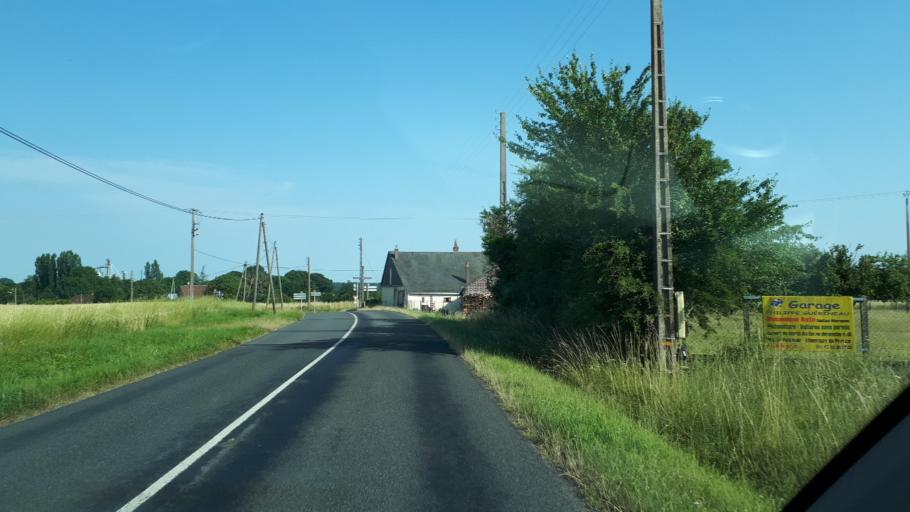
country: FR
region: Centre
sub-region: Departement du Loir-et-Cher
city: La Ville-aux-Clercs
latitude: 47.9592
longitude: 1.0729
